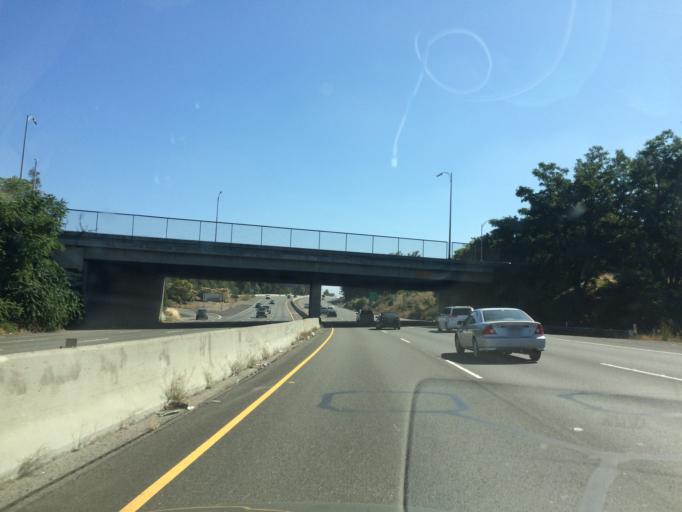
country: US
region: California
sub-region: Santa Clara County
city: Burbank
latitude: 37.3419
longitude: -121.9267
